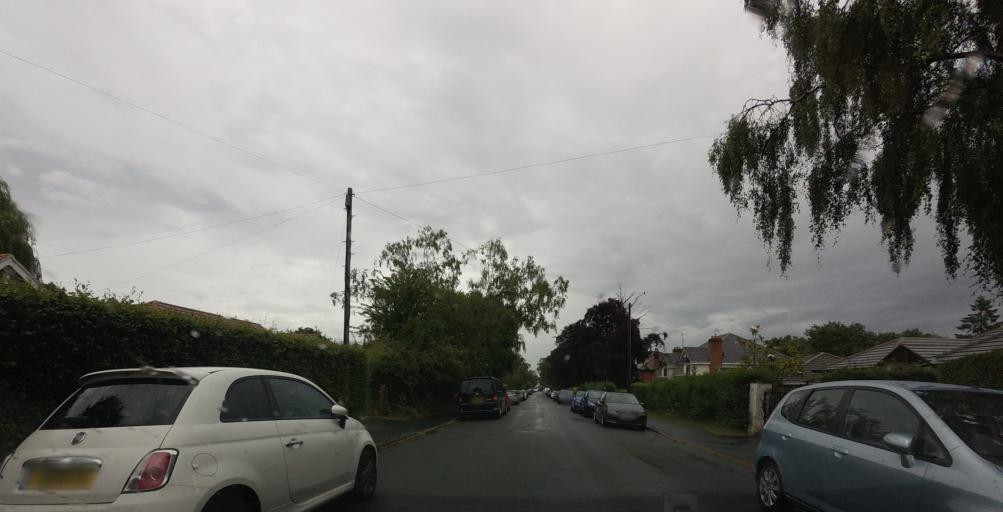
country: GB
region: England
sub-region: North Yorkshire
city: Harrogate
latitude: 53.9886
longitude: -1.5232
